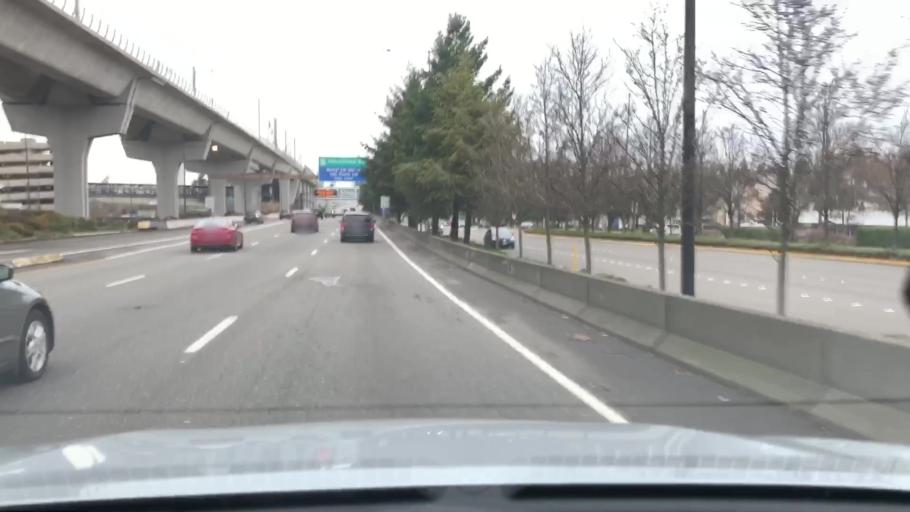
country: US
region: Washington
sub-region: King County
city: SeaTac
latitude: 47.4426
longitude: -122.2963
